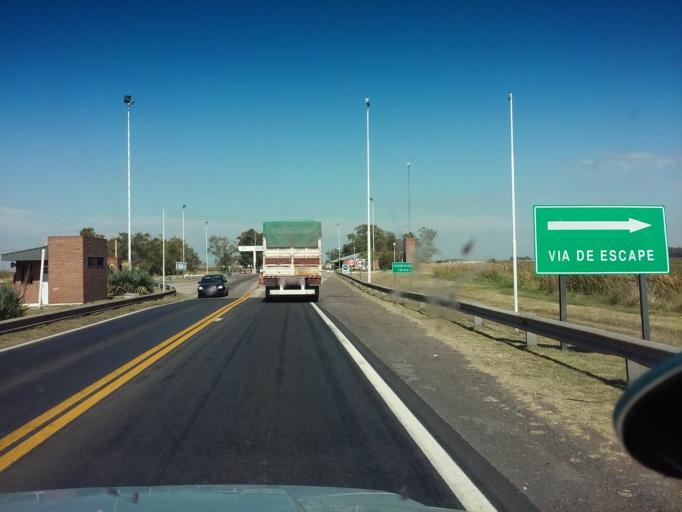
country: AR
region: Buenos Aires
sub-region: Partido de Nueve de Julio
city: Nueve de Julio
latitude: -35.3594
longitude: -60.7017
